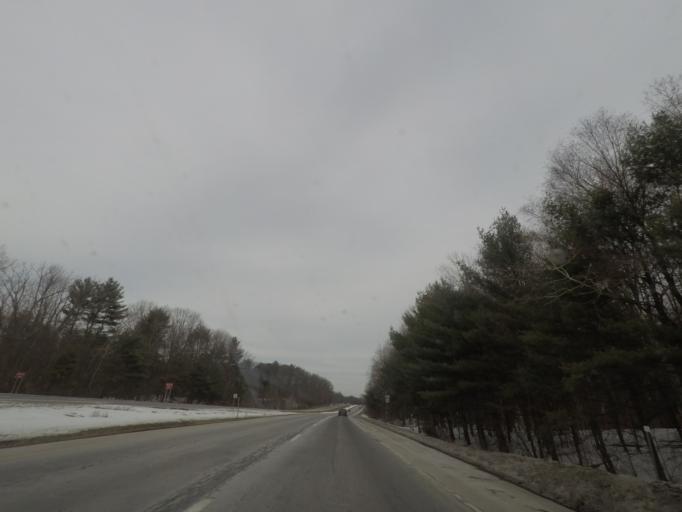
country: US
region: New York
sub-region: Albany County
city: Delmar
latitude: 42.6130
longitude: -73.8096
